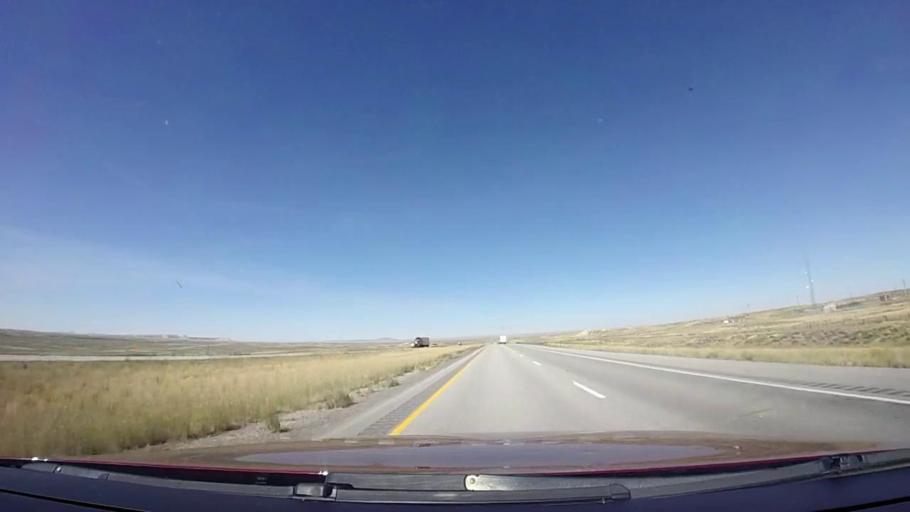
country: US
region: Wyoming
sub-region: Sweetwater County
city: Rock Springs
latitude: 41.6319
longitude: -108.3505
